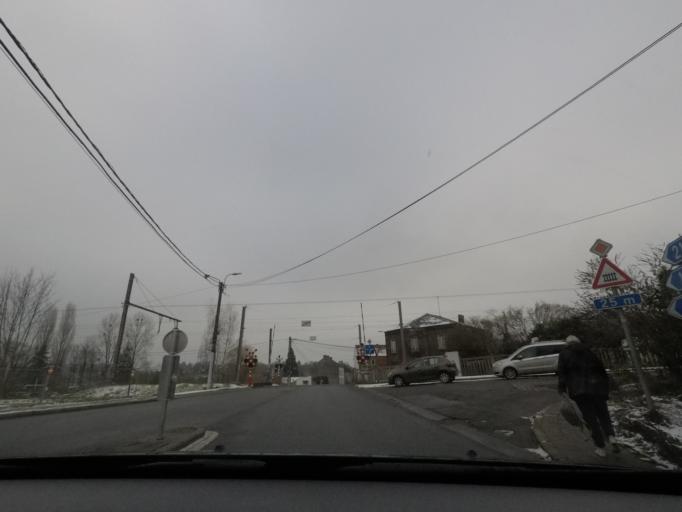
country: BE
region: Wallonia
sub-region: Province de Namur
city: Fosses-la-Ville
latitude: 50.4640
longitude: 4.6708
